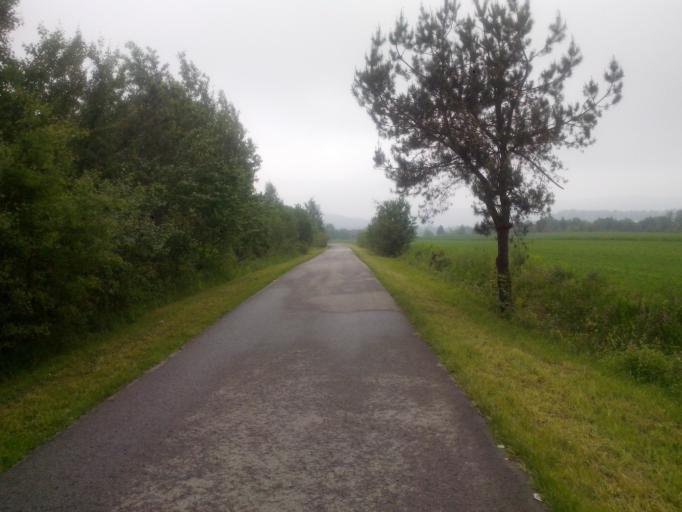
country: PL
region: Subcarpathian Voivodeship
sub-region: Powiat strzyzowski
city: Wysoka Strzyzowska
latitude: 49.8115
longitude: 21.7833
